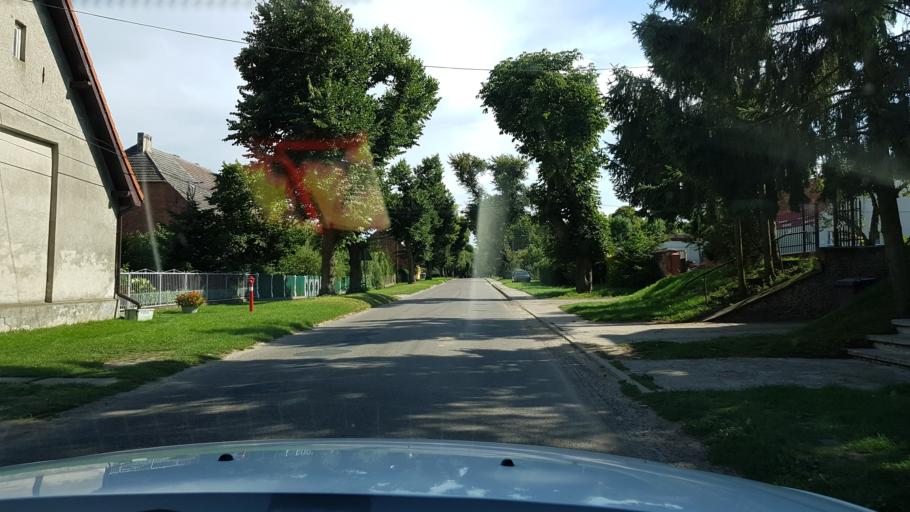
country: PL
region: West Pomeranian Voivodeship
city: Trzcinsko Zdroj
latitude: 52.9565
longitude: 14.5488
